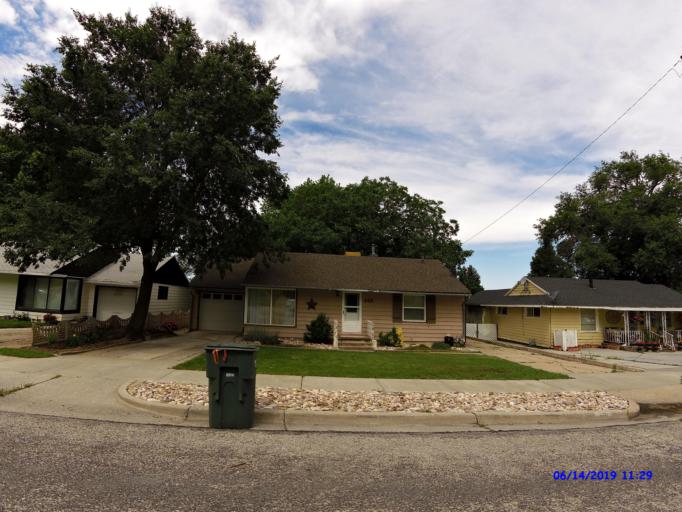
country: US
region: Utah
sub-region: Weber County
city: Ogden
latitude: 41.2547
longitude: -111.9425
